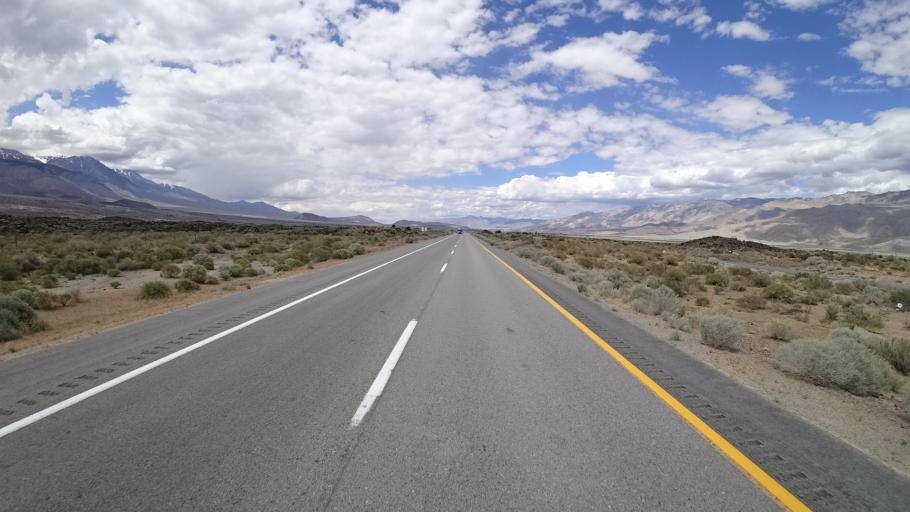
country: US
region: California
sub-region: Inyo County
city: Big Pine
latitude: 36.9366
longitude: -118.2410
